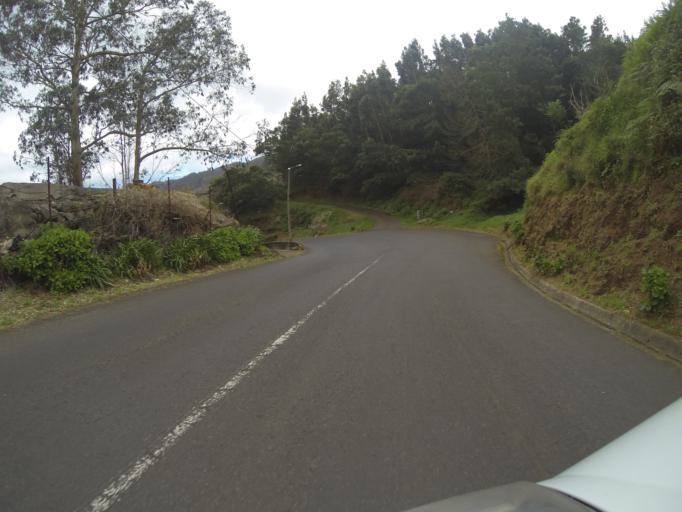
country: PT
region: Madeira
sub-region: Santa Cruz
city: Santa Cruz
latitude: 32.7354
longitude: -16.8198
